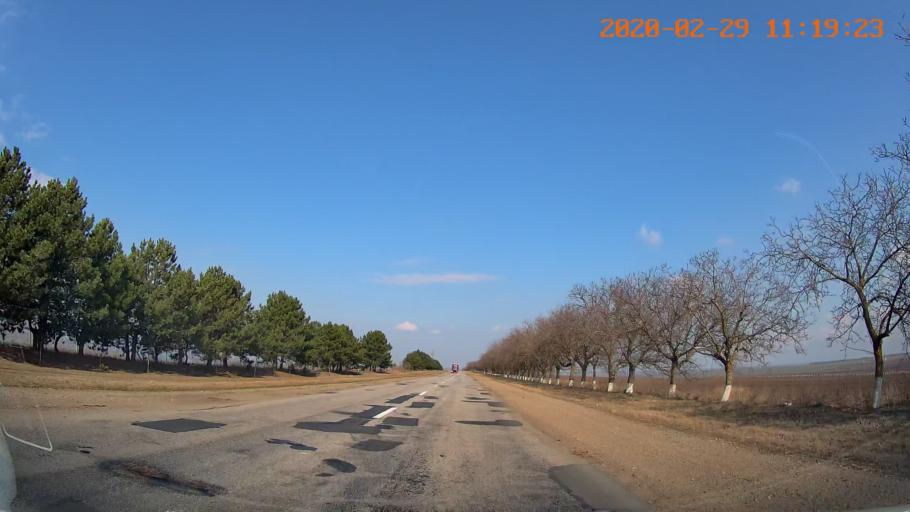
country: MD
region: Telenesti
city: Cocieri
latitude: 47.3490
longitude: 29.1749
